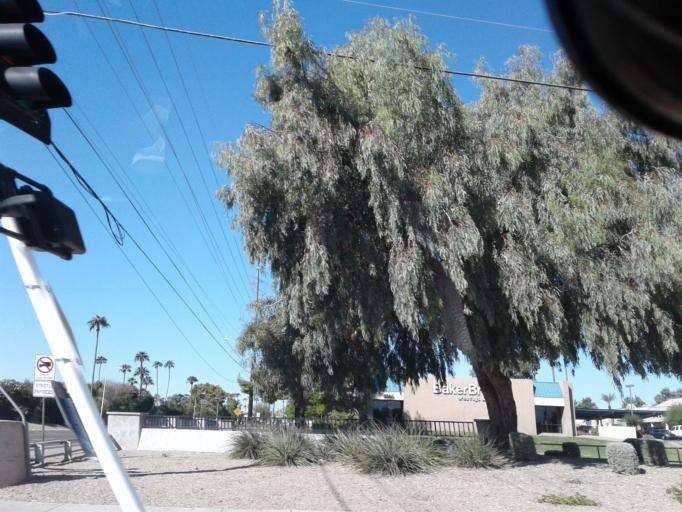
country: US
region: Arizona
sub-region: Maricopa County
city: Scottsdale
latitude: 33.5098
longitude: -111.9088
